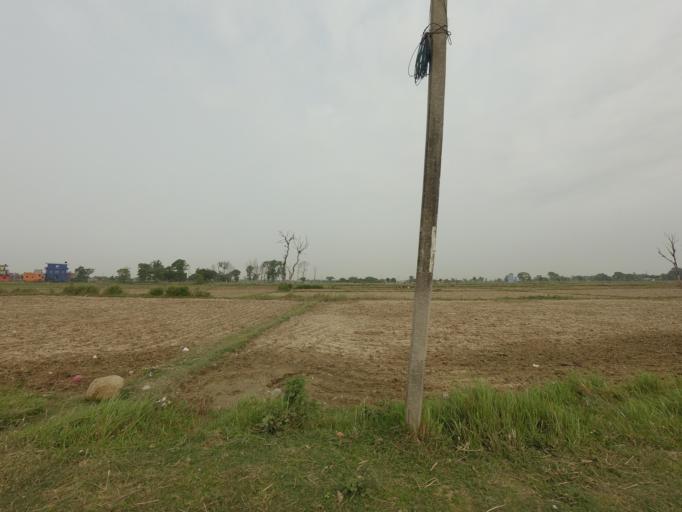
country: NP
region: Western Region
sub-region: Lumbini Zone
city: Bhairahawa
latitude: 27.4883
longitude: 83.4279
